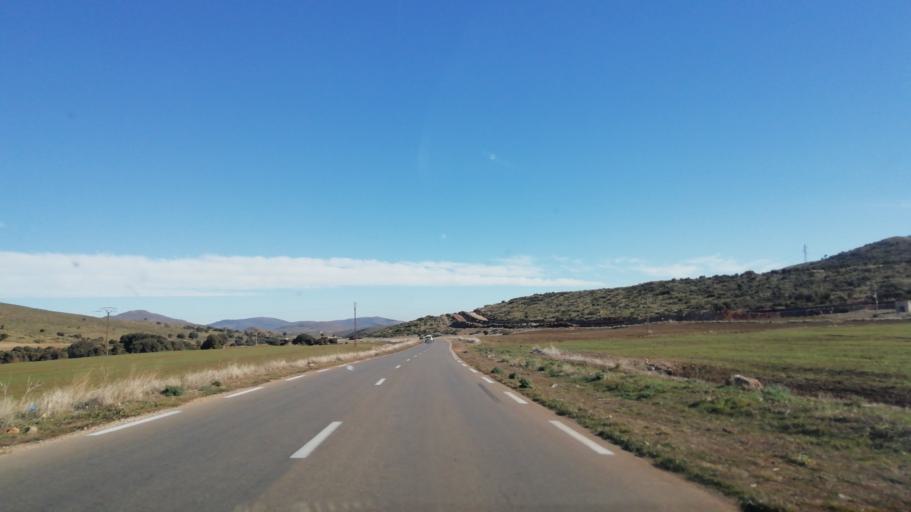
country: DZ
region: Tlemcen
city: Ouled Mimoun
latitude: 34.7489
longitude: -1.1597
